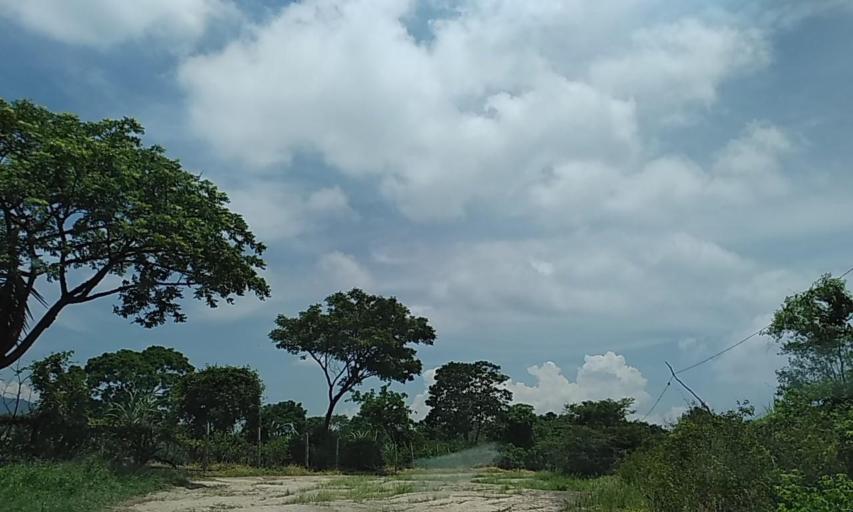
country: MX
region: Veracruz
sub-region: Emiliano Zapata
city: Dos Rios
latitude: 19.4382
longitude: -96.7491
